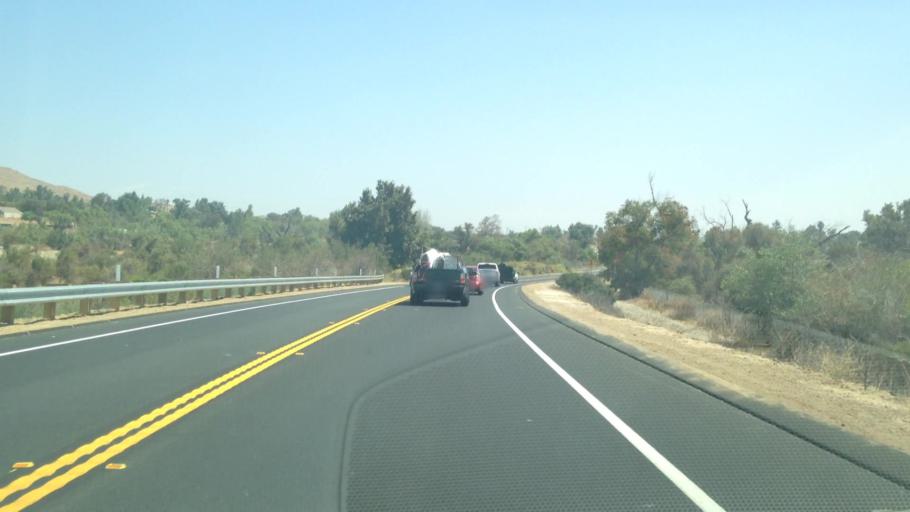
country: US
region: California
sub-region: Riverside County
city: Woodcrest
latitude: 33.8328
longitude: -117.3567
